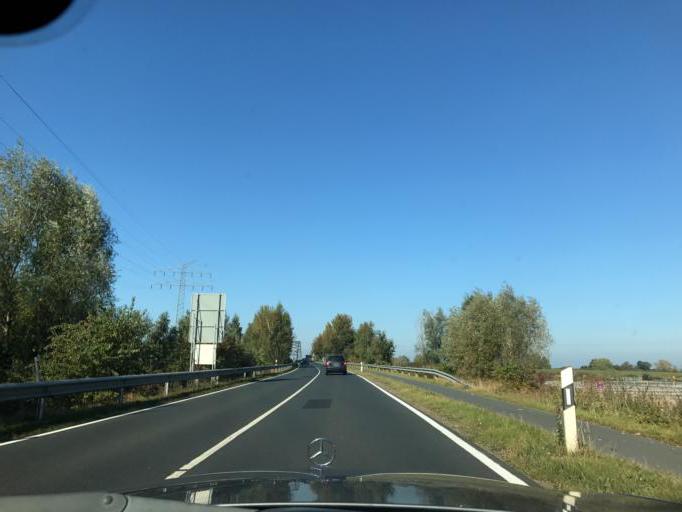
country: DE
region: Lower Saxony
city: Papenburg
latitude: 53.0995
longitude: 7.3541
